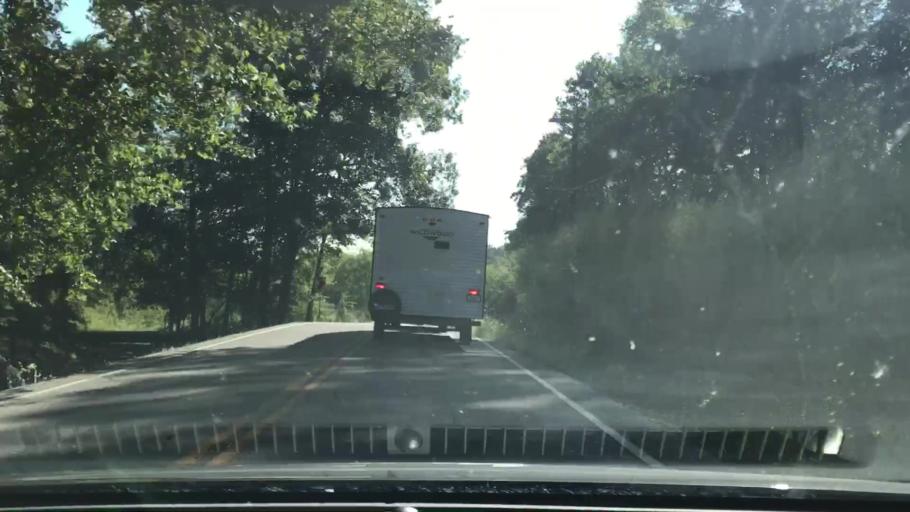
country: US
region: Tennessee
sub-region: Smith County
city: Carthage
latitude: 36.3485
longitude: -85.8369
